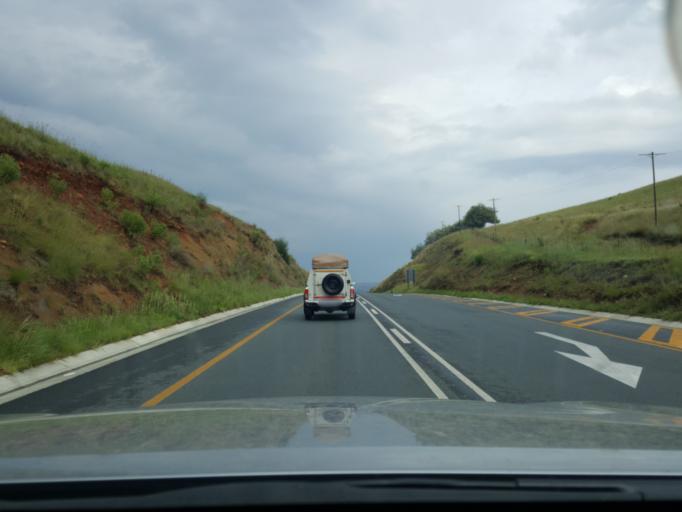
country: ZA
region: Mpumalanga
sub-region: Nkangala District Municipality
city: Belfast
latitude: -25.6262
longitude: 30.3125
